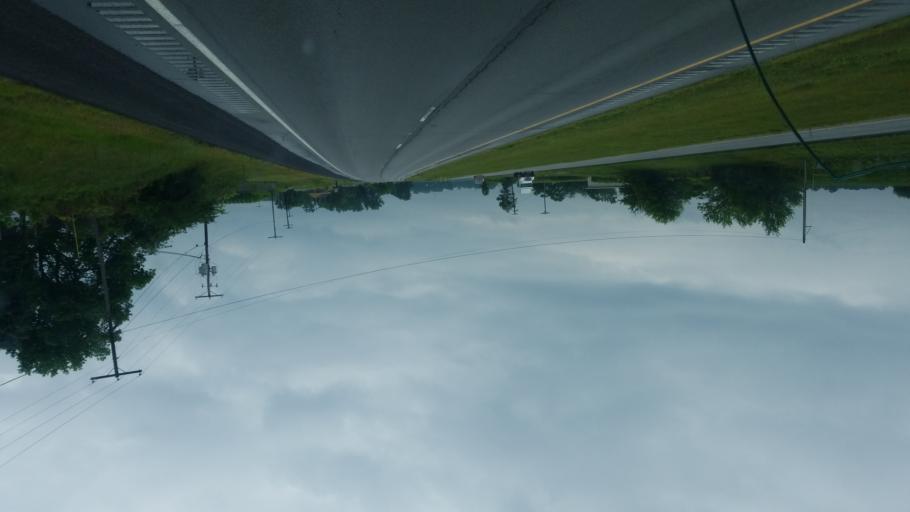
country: US
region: Indiana
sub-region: Allen County
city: New Haven
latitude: 40.9644
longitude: -85.0762
